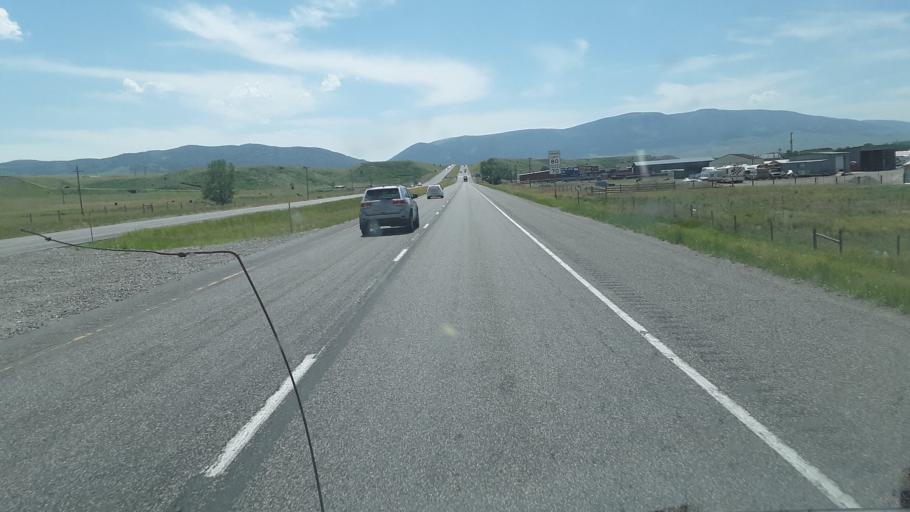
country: US
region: Montana
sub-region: Park County
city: Livingston
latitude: 45.6822
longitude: -110.5084
